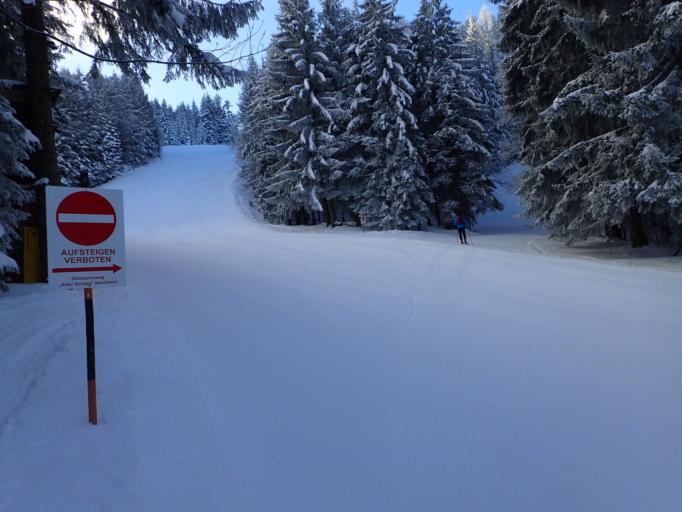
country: AT
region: Salzburg
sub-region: Politischer Bezirk Hallein
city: Hallein
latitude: 47.6406
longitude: 13.0970
